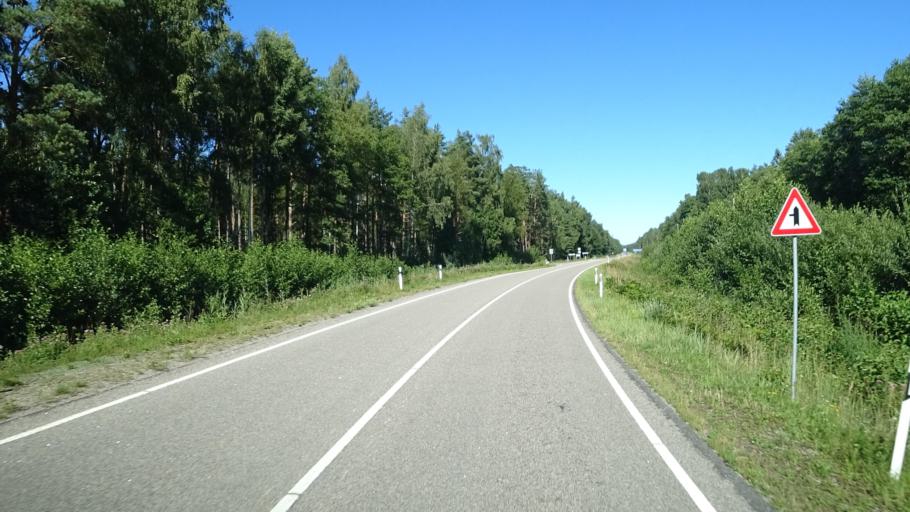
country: LV
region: Dundaga
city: Dundaga
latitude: 57.6862
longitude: 22.3679
